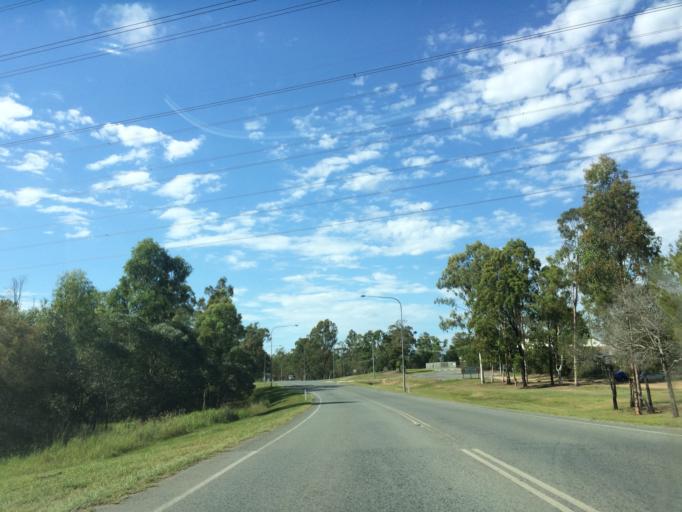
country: AU
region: Queensland
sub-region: Logan
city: Park Ridge South
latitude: -27.7286
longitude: 152.9841
